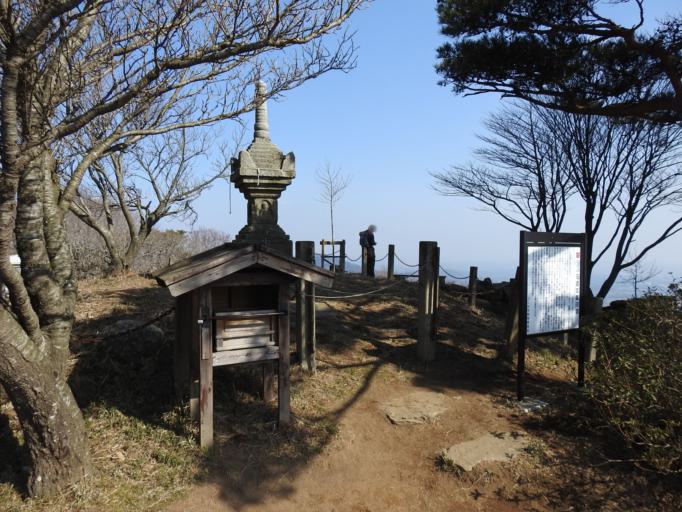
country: JP
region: Ibaraki
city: Tsukuba
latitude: 36.1676
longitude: 140.1299
